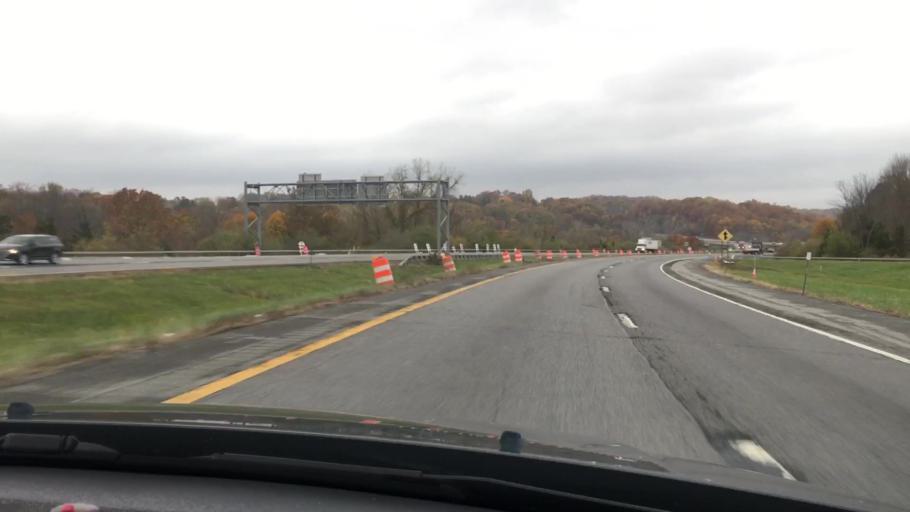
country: US
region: New York
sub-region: Putnam County
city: Brewster
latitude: 41.3927
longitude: -73.5997
